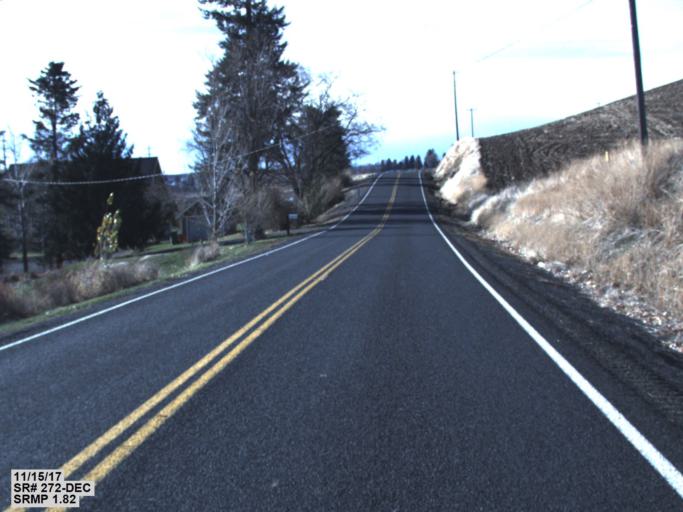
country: US
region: Washington
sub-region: Whitman County
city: Colfax
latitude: 46.8910
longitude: -117.3328
